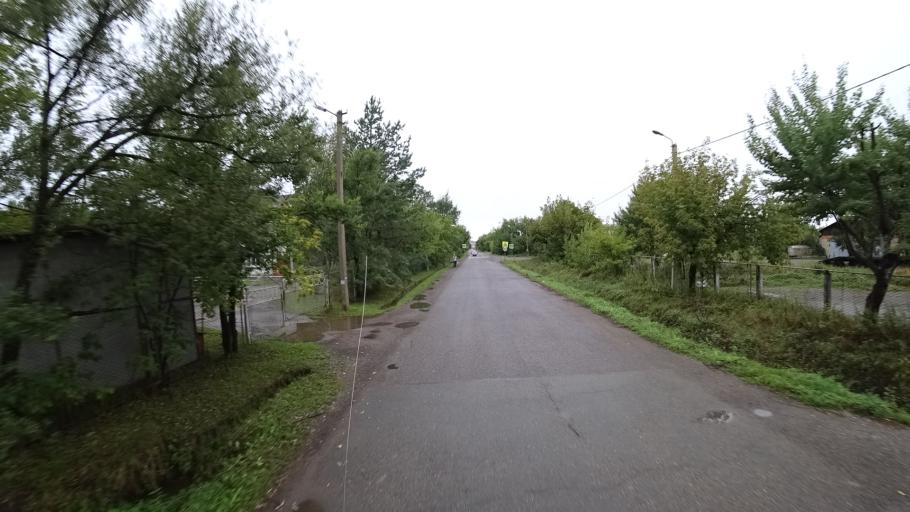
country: RU
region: Primorskiy
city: Monastyrishche
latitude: 44.2030
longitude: 132.4591
